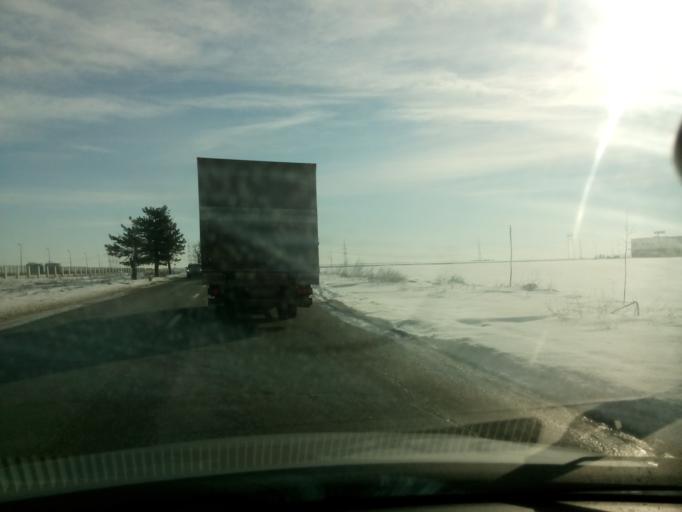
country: RO
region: Ilfov
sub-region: Comuna Berceni
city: Berceni
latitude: 44.3538
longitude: 26.2110
